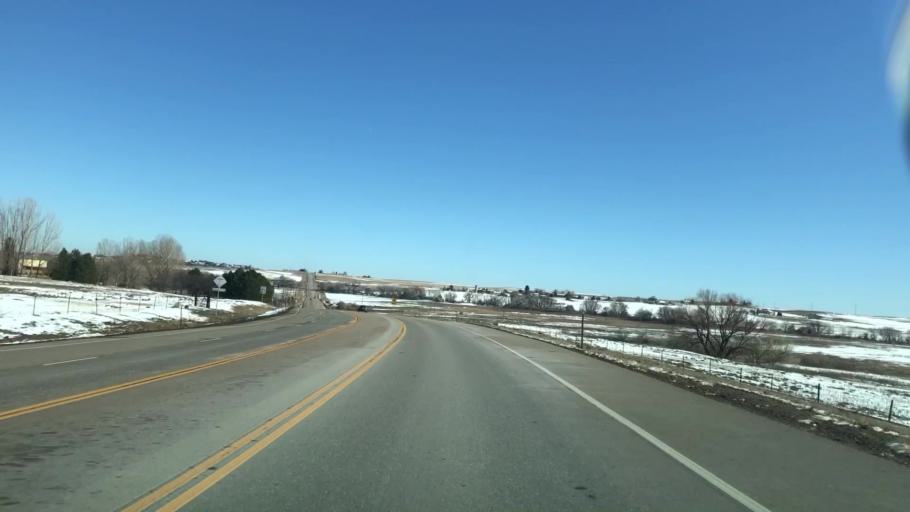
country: US
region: Colorado
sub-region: Boulder County
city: Niwot
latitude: 40.0869
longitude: -105.1858
